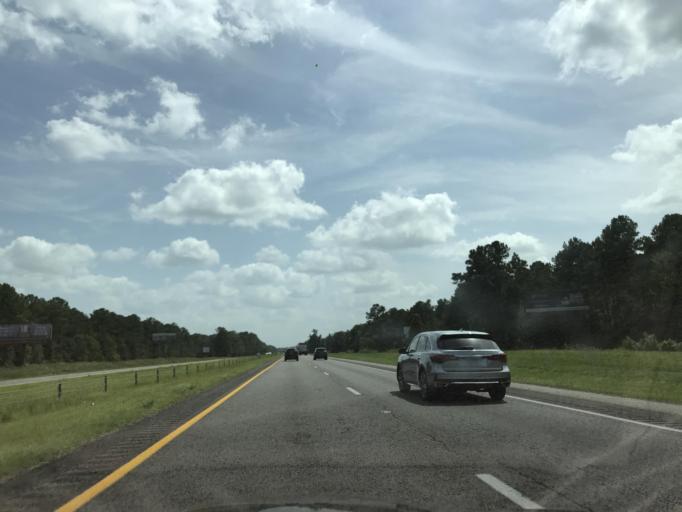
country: US
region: North Carolina
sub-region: Duplin County
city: Wallace
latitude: 34.6526
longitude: -77.9413
